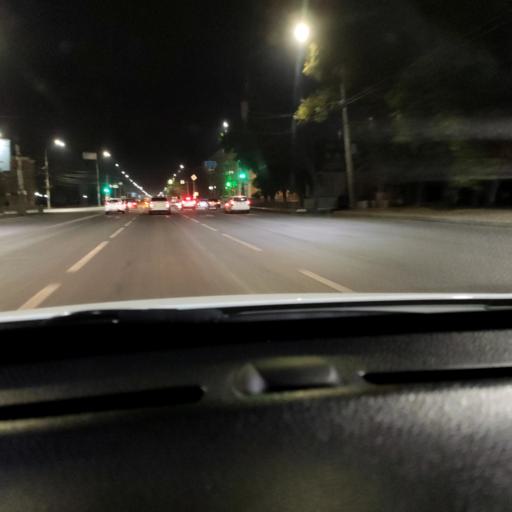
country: RU
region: Voronezj
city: Voronezh
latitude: 51.6324
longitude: 39.2319
